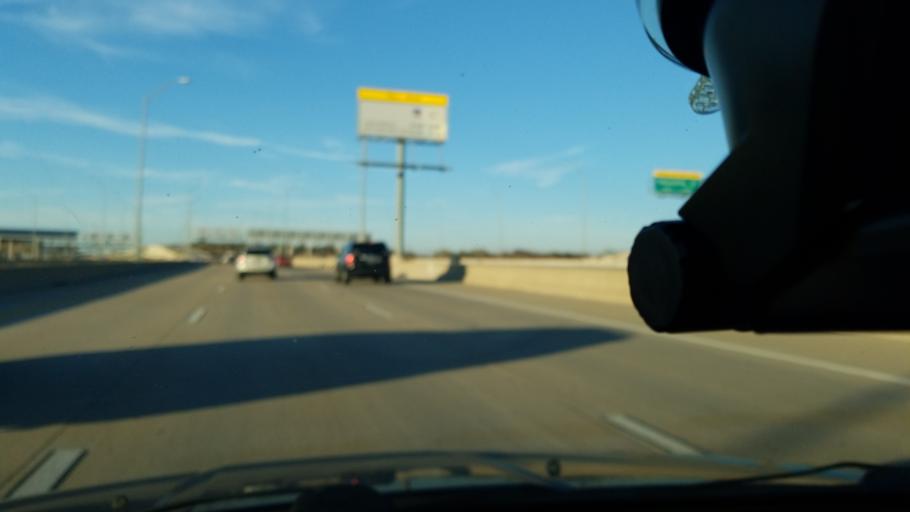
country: US
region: Texas
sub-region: Travis County
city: Wells Branch
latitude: 30.4508
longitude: -97.6962
